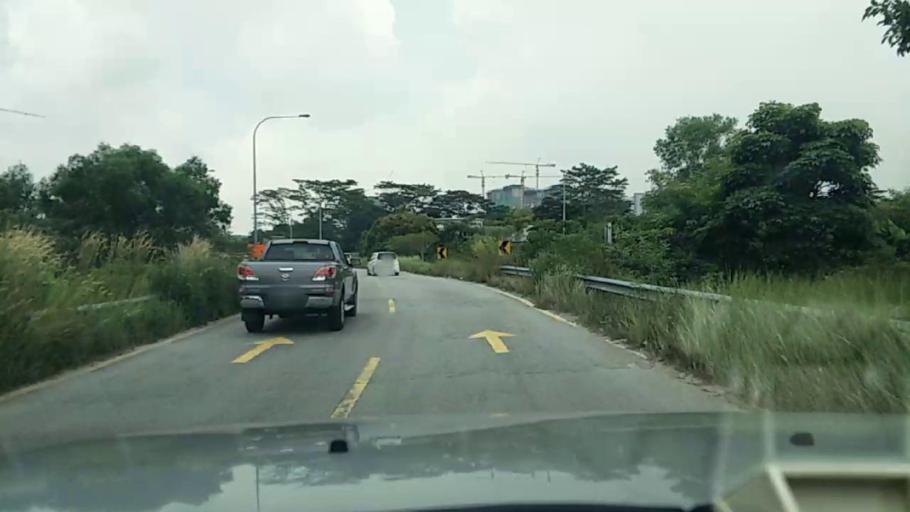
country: MY
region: Putrajaya
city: Putrajaya
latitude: 2.9300
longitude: 101.6233
